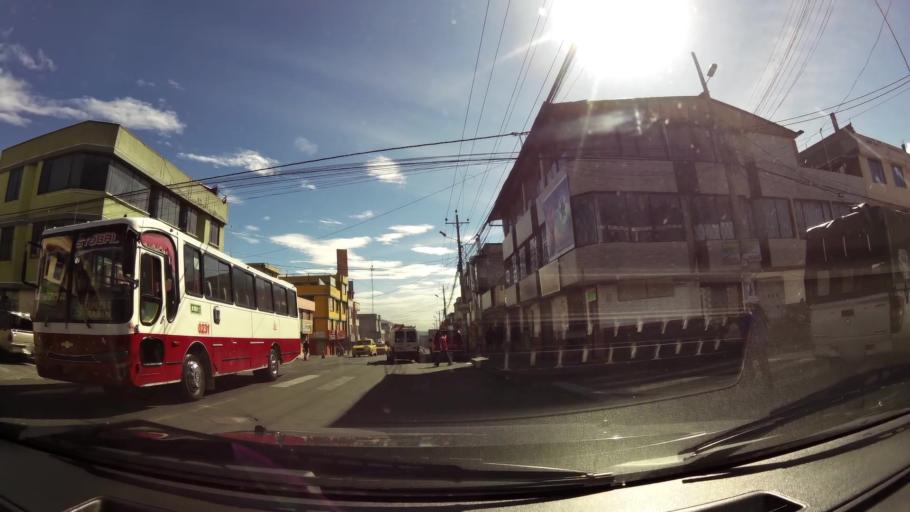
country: EC
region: Pichincha
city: Quito
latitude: -0.2975
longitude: -78.5646
